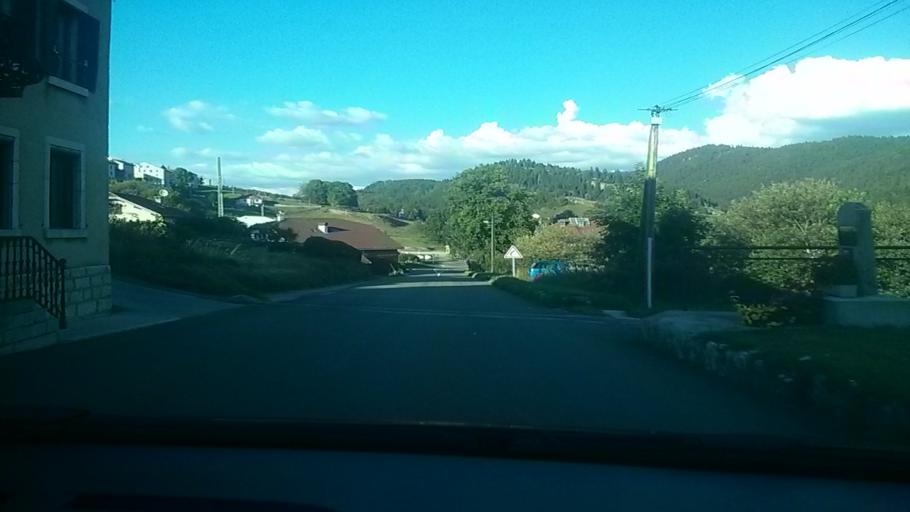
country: FR
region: Franche-Comte
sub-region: Departement du Jura
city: Saint-Claude
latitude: 46.3683
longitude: 5.9121
